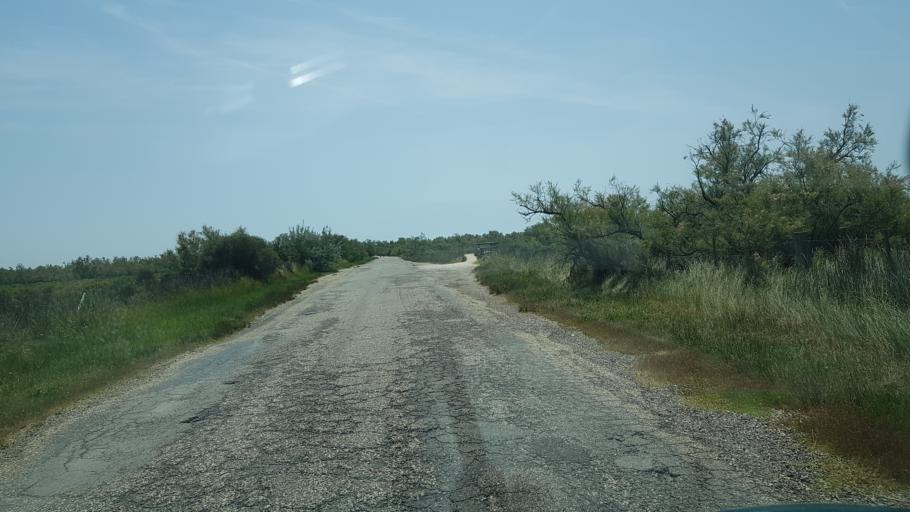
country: FR
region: Provence-Alpes-Cote d'Azur
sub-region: Departement des Bouches-du-Rhone
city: Arles
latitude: 43.5401
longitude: 4.6372
